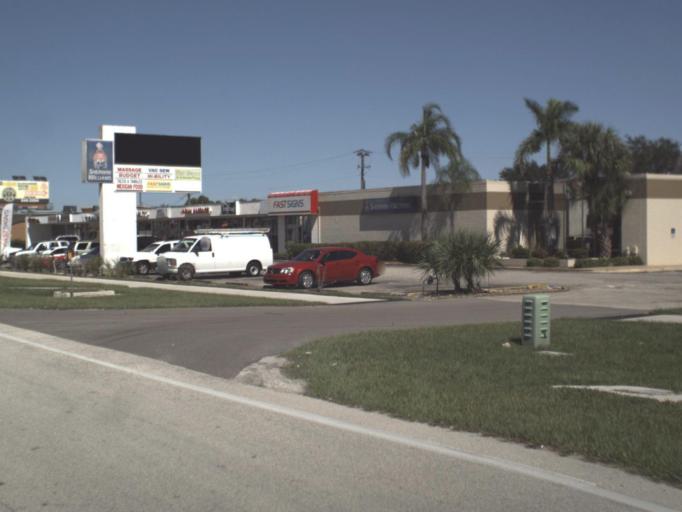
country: US
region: Florida
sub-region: Lee County
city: Pine Manor
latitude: 26.5650
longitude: -81.8718
